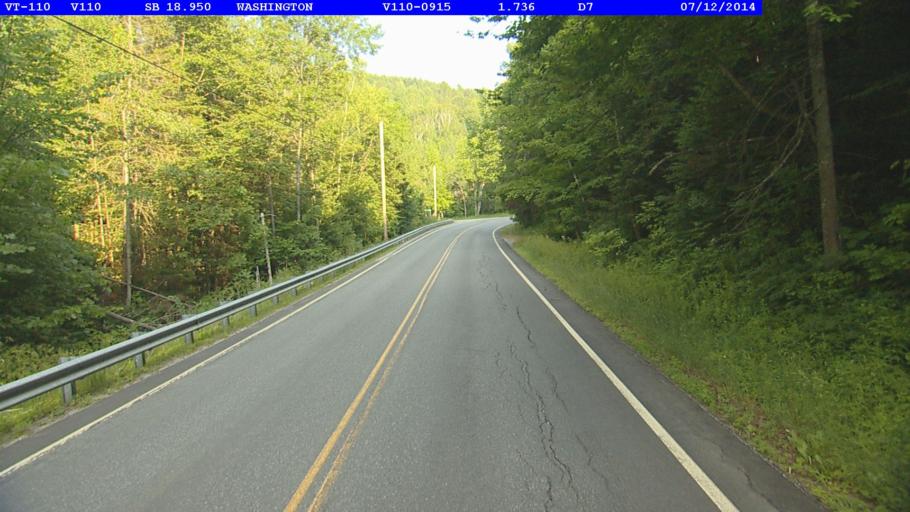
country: US
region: Vermont
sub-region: Orange County
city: Chelsea
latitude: 44.0618
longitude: -72.4643
